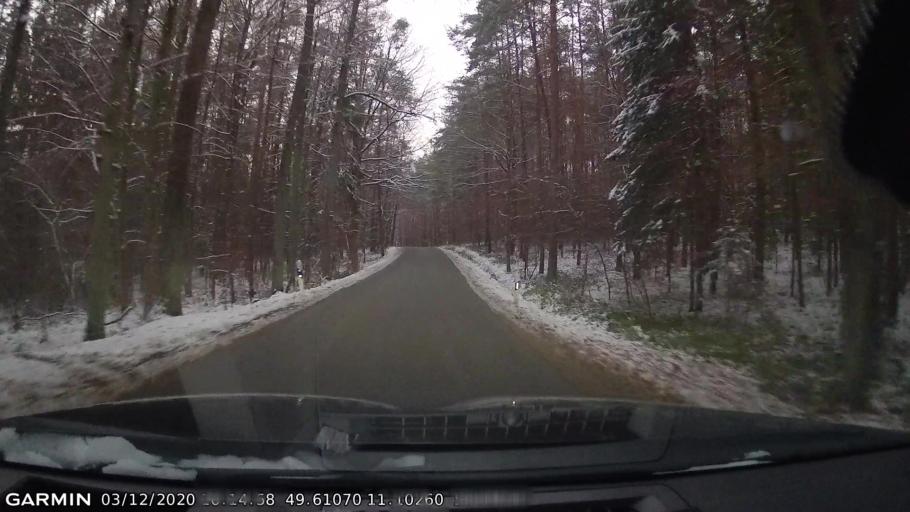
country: DE
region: Bavaria
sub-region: Upper Franconia
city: Dormitz
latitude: 49.6107
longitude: 11.1026
